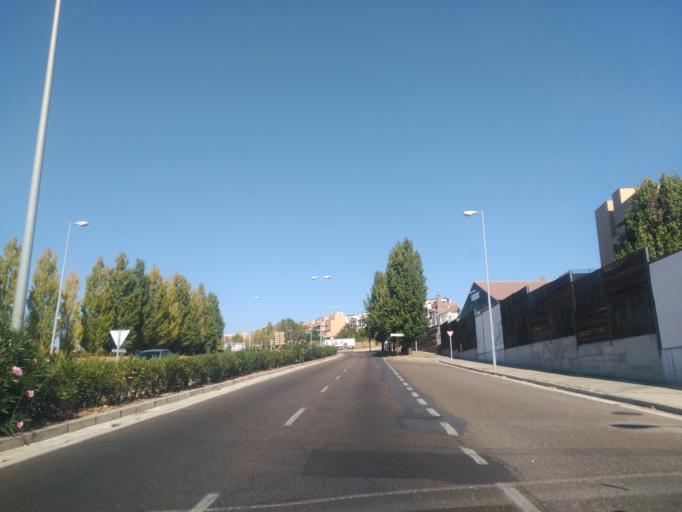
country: ES
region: Castille and Leon
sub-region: Provincia de Valladolid
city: Zaratan
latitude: 41.6285
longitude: -4.7595
